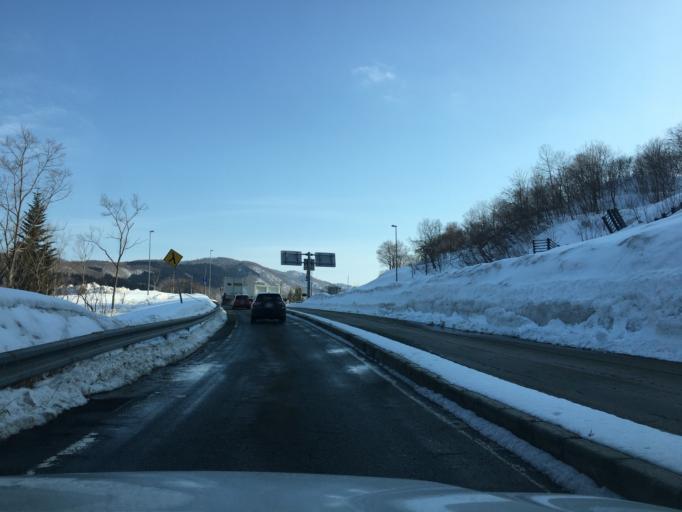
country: JP
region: Yamagata
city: Sagae
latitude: 38.4554
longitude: 139.9922
